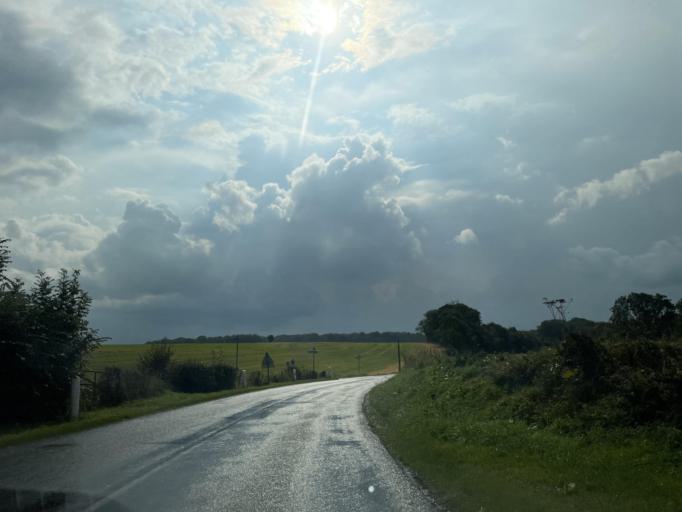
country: FR
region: Haute-Normandie
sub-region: Departement de la Seine-Maritime
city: Envermeu
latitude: 49.9099
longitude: 1.2770
